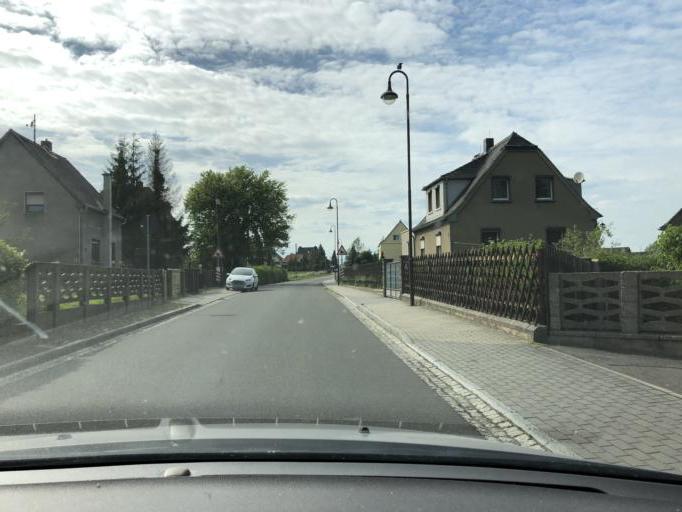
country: DE
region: Saxony
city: Grimma
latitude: 51.2748
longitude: 12.7108
